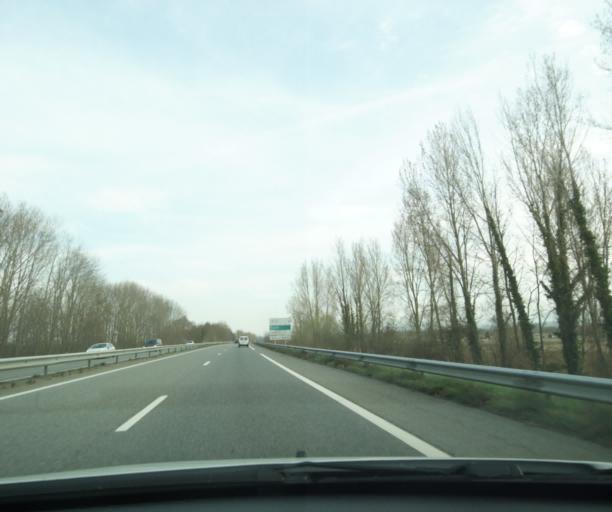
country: FR
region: Midi-Pyrenees
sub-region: Departement des Hautes-Pyrenees
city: Juillan
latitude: 43.2161
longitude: 0.0272
